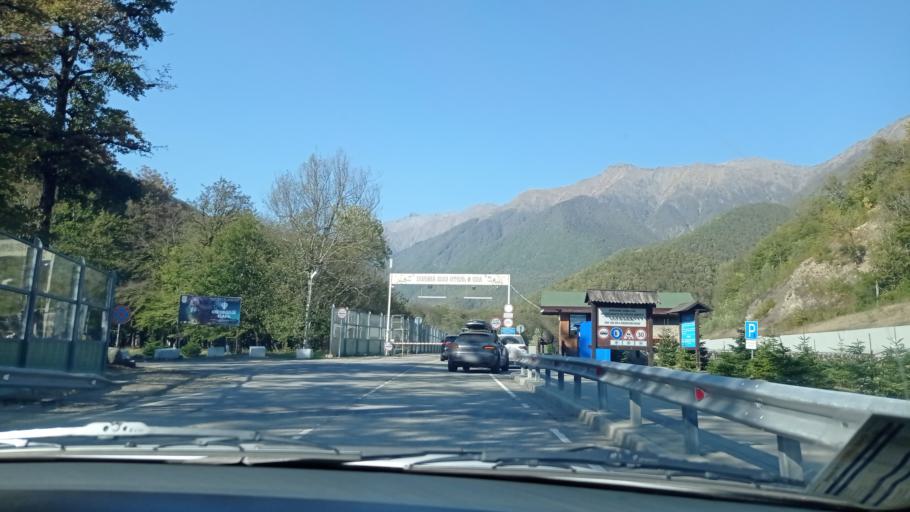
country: RU
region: Krasnodarskiy
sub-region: Sochi City
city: Krasnaya Polyana
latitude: 43.6969
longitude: 40.2690
